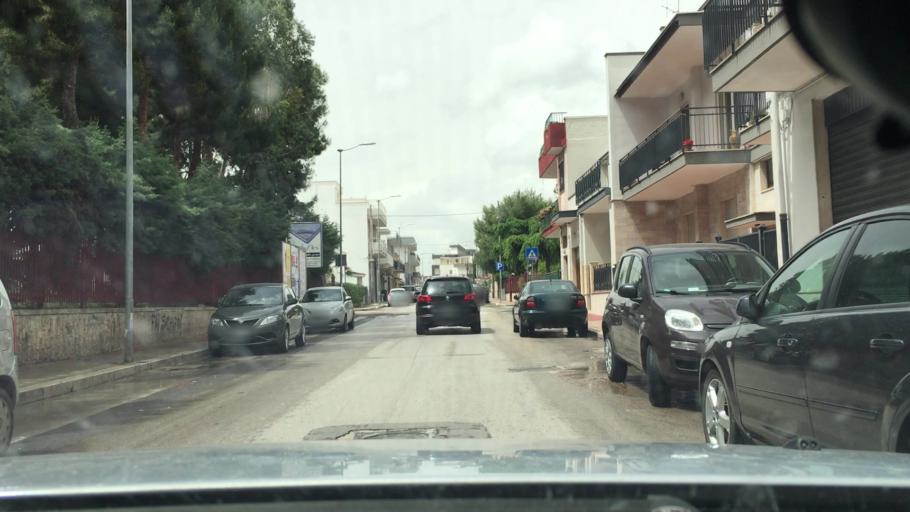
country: IT
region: Apulia
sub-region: Provincia di Bari
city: Capurso
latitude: 41.0500
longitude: 16.9199
